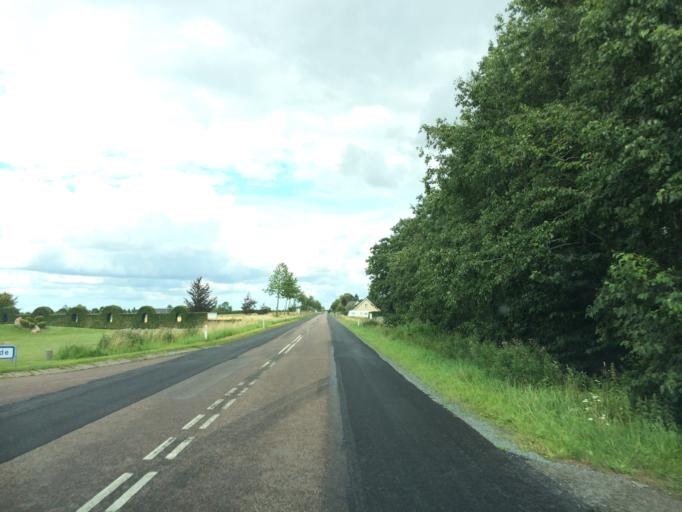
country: DK
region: South Denmark
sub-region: Assens Kommune
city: Tommerup
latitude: 55.2576
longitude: 10.2461
